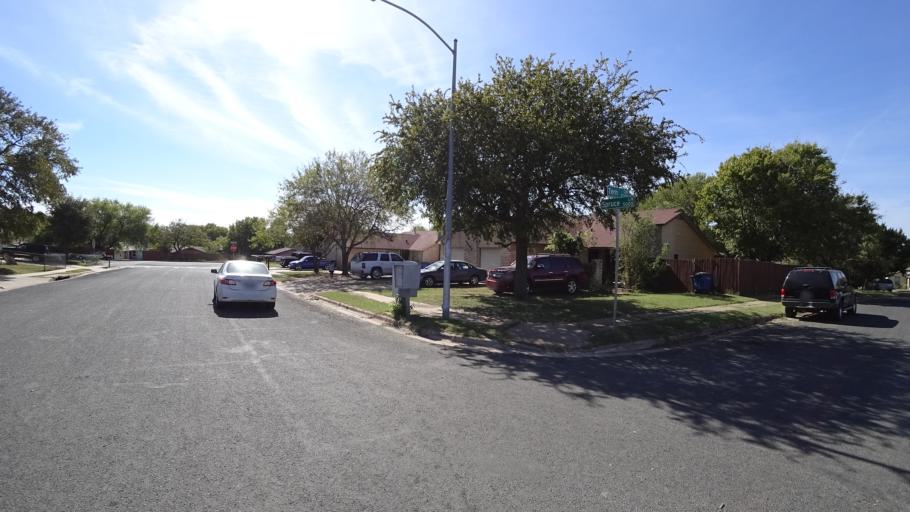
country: US
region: Texas
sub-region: Travis County
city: Austin
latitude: 30.2005
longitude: -97.7484
